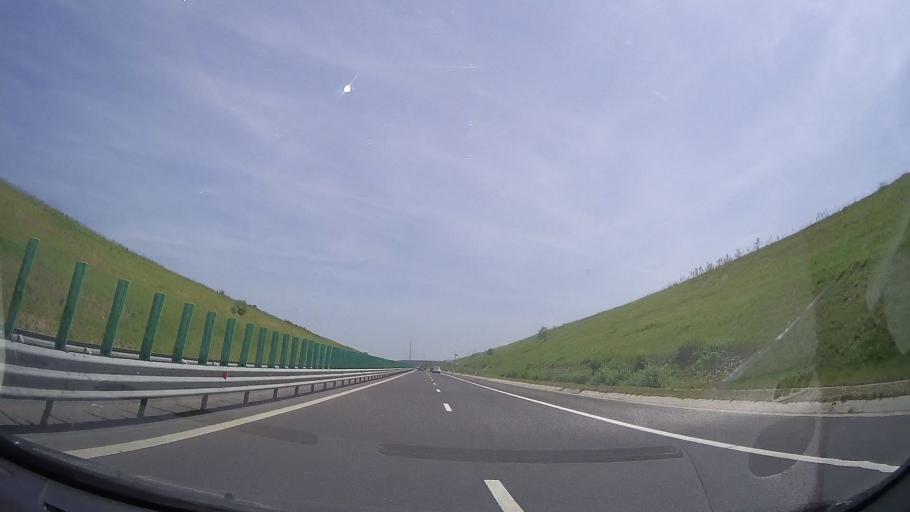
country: RO
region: Alba
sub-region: Comuna Saliste
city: Salistea
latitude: 45.9410
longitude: 23.4014
